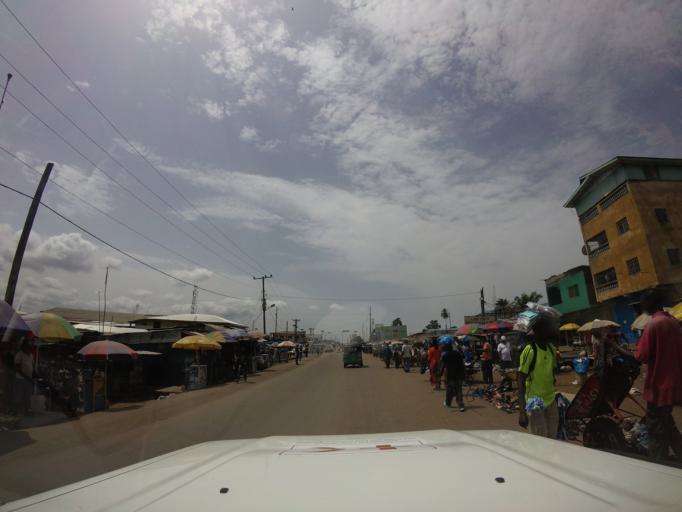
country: LR
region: Montserrado
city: Monrovia
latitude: 6.3689
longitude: -10.7881
